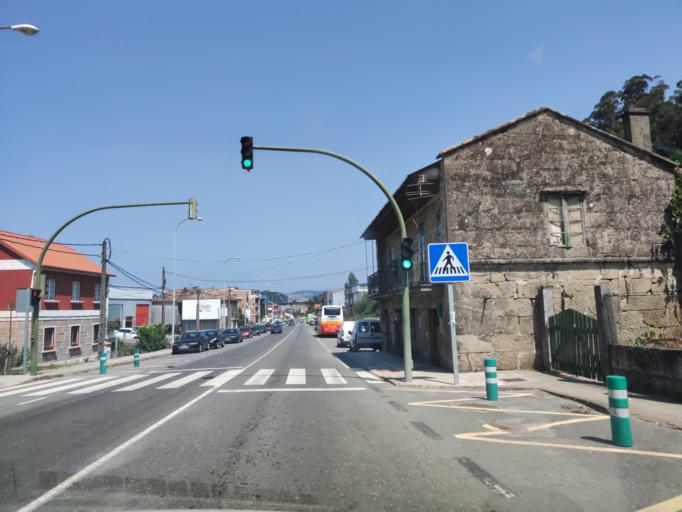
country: ES
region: Galicia
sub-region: Provincia de Pontevedra
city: Redondela
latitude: 42.2721
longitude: -8.6102
